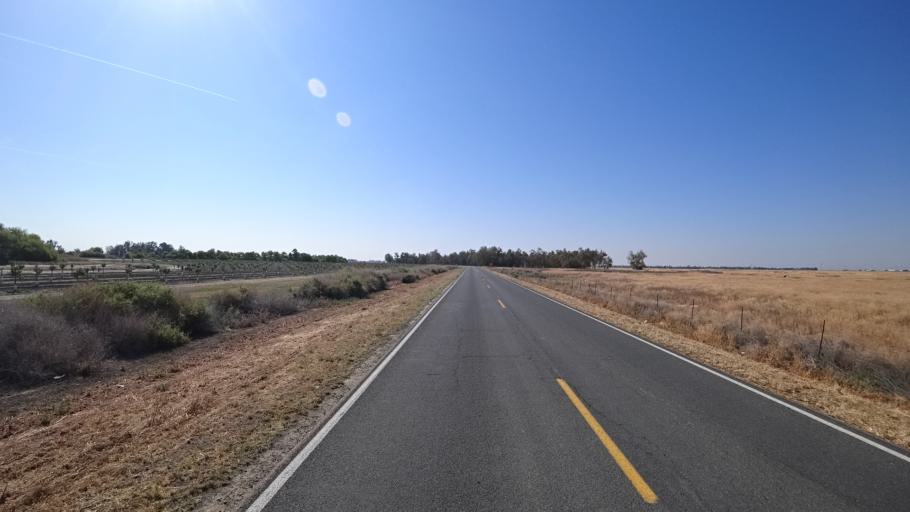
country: US
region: California
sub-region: Fresno County
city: Riverdale
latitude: 36.3654
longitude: -119.9175
